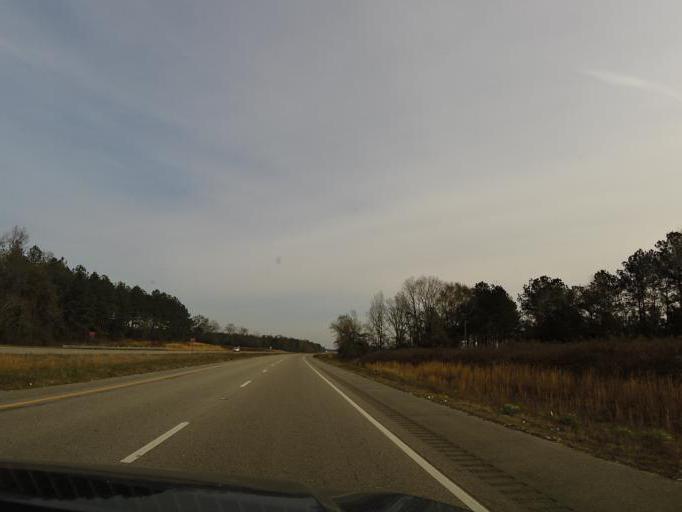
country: US
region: Alabama
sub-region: Houston County
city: Ashford
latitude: 31.1341
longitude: -85.1256
